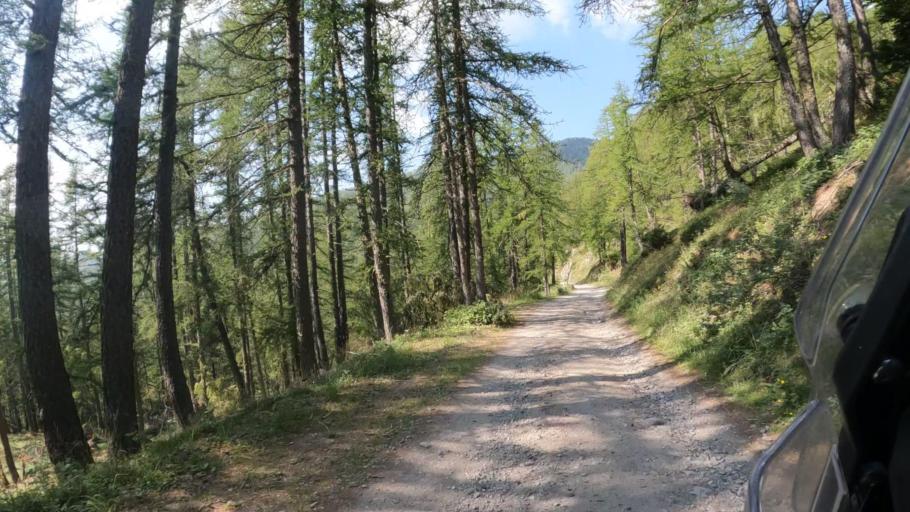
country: IT
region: Piedmont
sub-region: Provincia di Cuneo
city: Briga Alta
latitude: 44.1010
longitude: 7.7186
